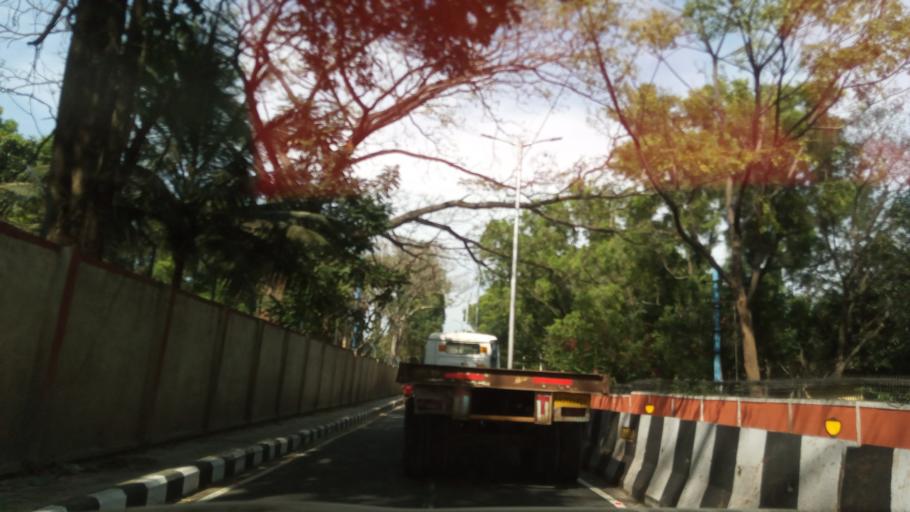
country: IN
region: Karnataka
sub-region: Bangalore Urban
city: Bangalore
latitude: 13.0358
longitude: 77.5414
